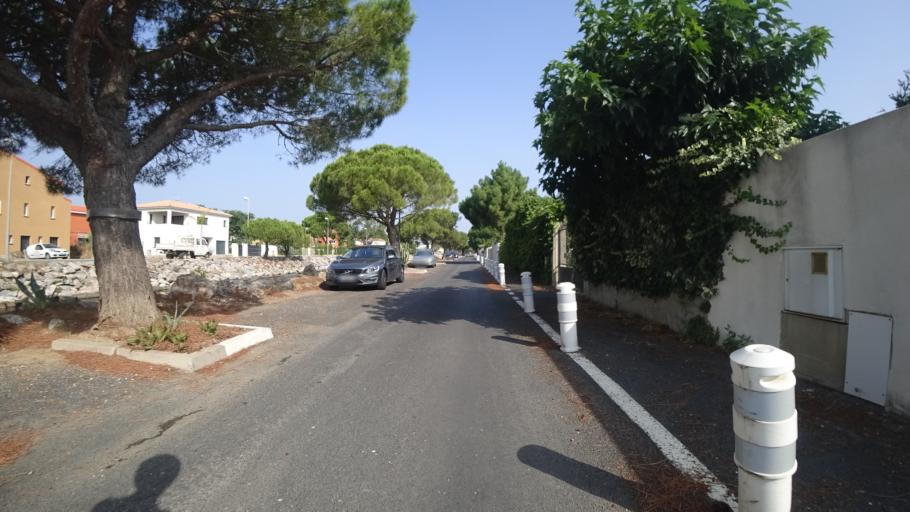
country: FR
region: Languedoc-Roussillon
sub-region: Departement des Pyrenees-Orientales
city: Sainte-Marie-Plage
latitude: 42.7248
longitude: 3.0339
